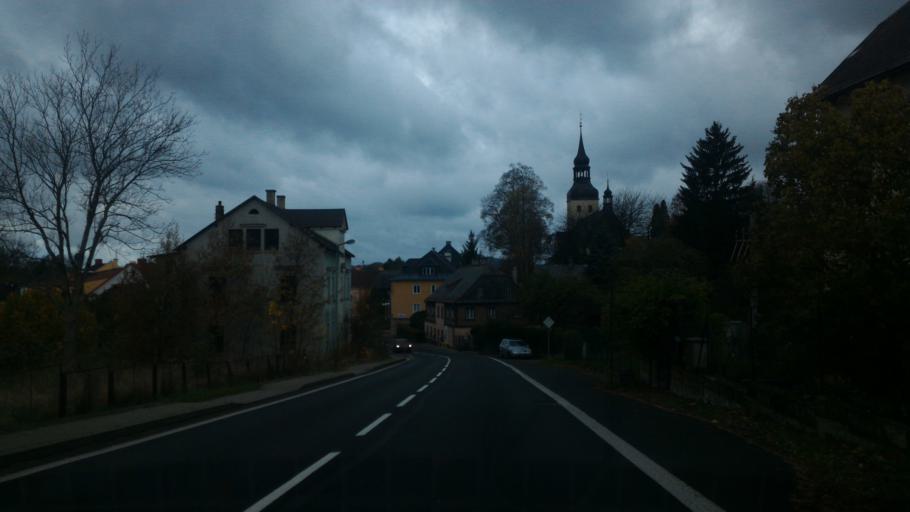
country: CZ
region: Ustecky
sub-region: Okres Decin
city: Chribska
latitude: 50.8635
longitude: 14.4851
